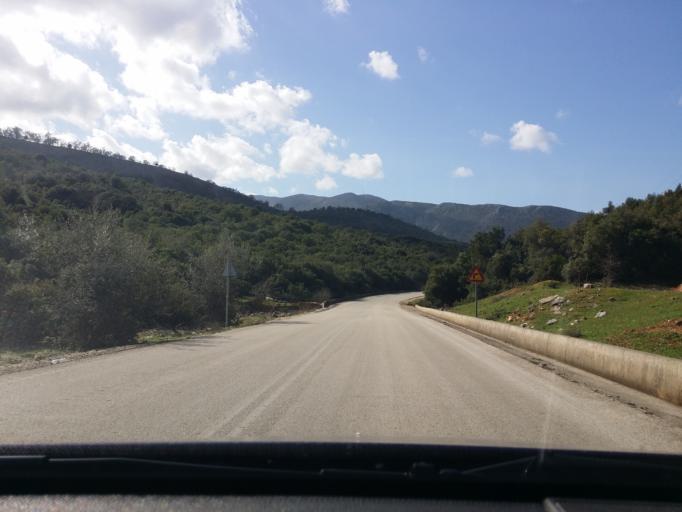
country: GR
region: West Greece
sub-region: Nomos Aitolias kai Akarnanias
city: Astakos
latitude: 38.5996
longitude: 21.1088
